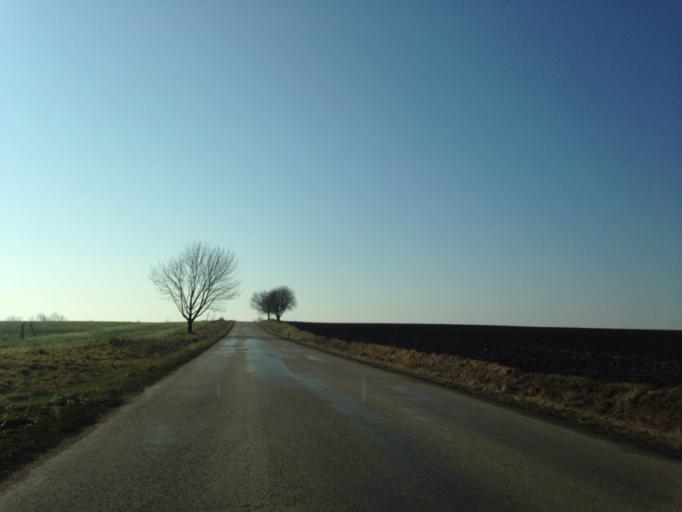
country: SK
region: Nitriansky
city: Svodin
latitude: 47.9447
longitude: 18.4138
